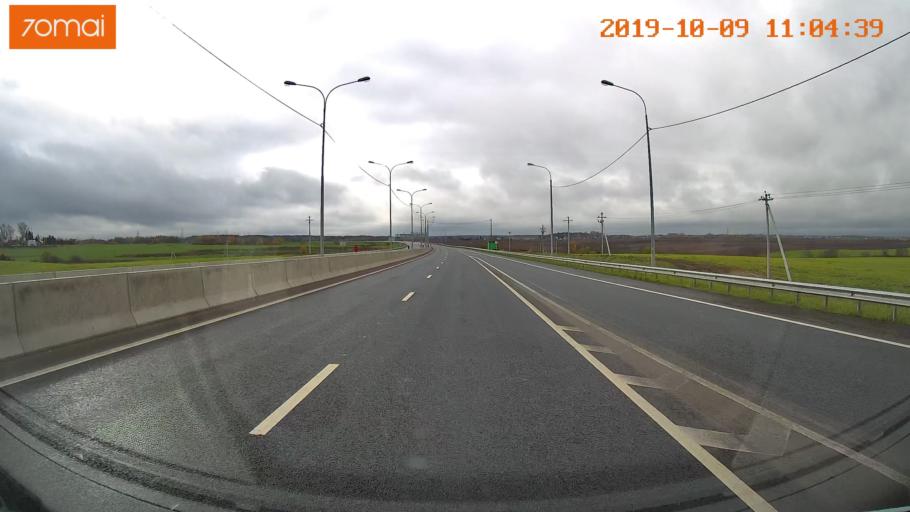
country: RU
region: Vologda
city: Molochnoye
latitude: 59.2099
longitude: 39.7655
